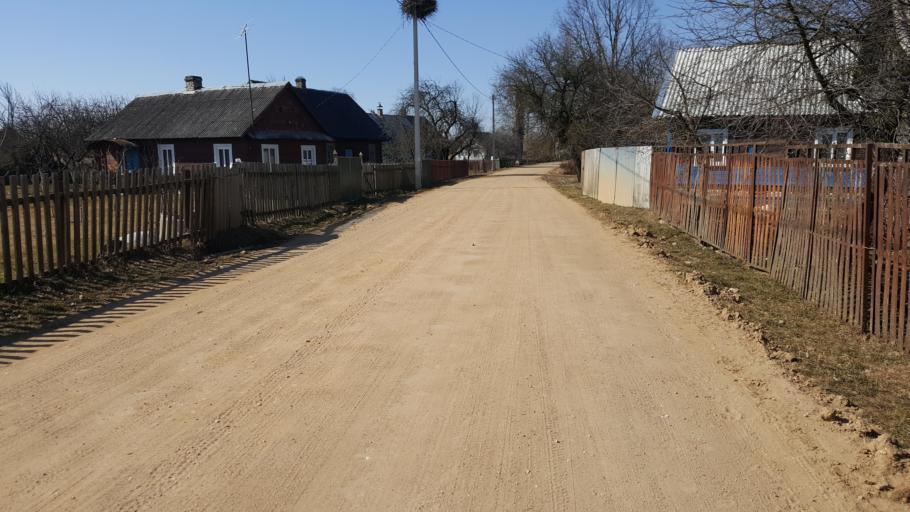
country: BY
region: Brest
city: Kamyanyets
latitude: 52.3727
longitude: 23.7840
